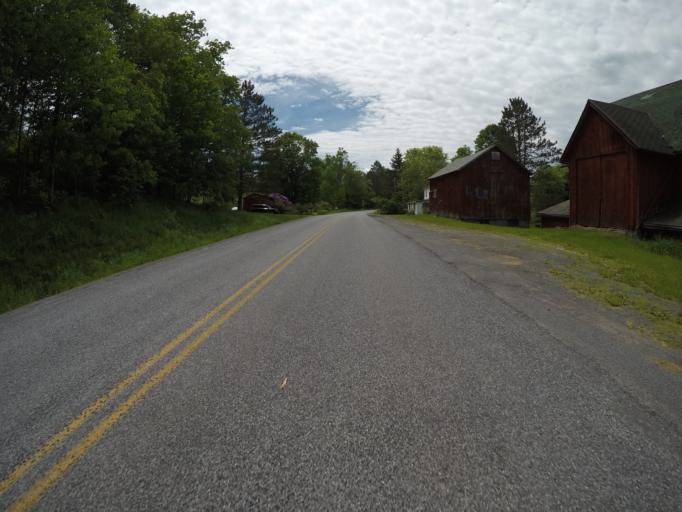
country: US
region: New York
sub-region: Delaware County
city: Stamford
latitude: 42.2317
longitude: -74.5610
